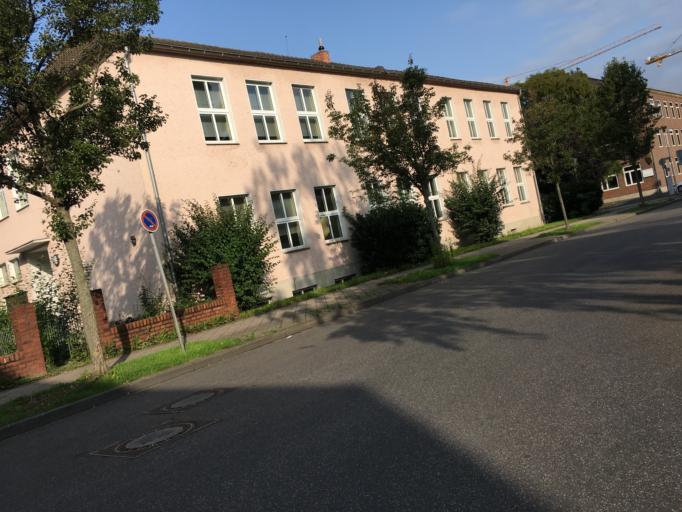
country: DE
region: North Rhine-Westphalia
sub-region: Regierungsbezirk Koln
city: Dueren
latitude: 50.8046
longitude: 6.4891
